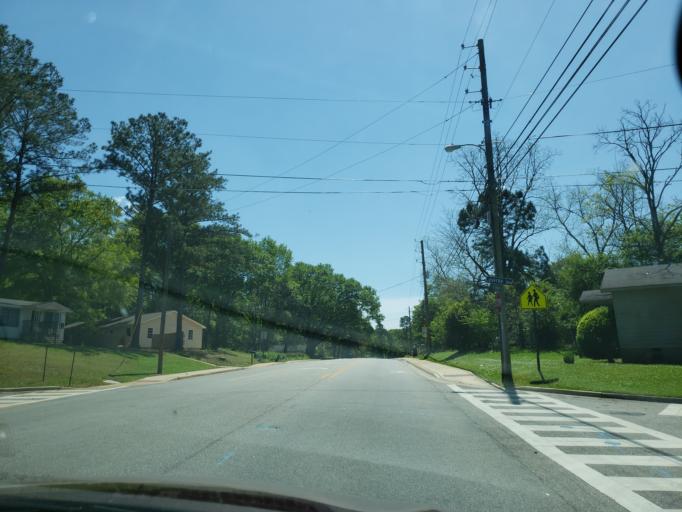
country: US
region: Alabama
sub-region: Lee County
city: Auburn
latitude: 32.6208
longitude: -85.4923
